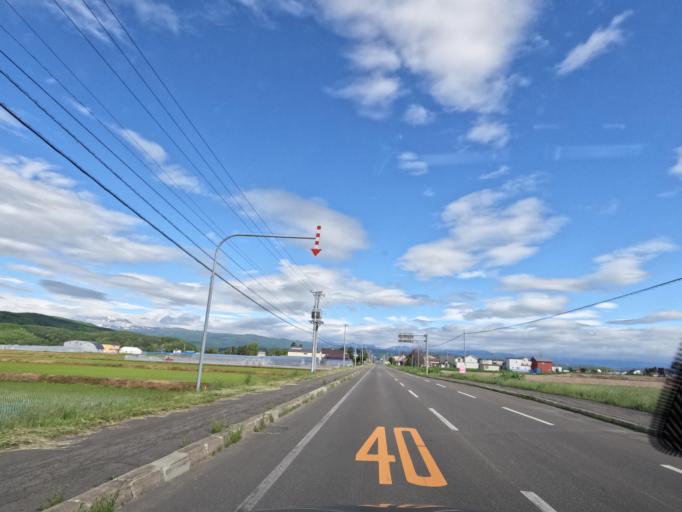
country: JP
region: Hokkaido
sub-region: Asahikawa-shi
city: Asahikawa
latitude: 43.7204
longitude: 142.5234
